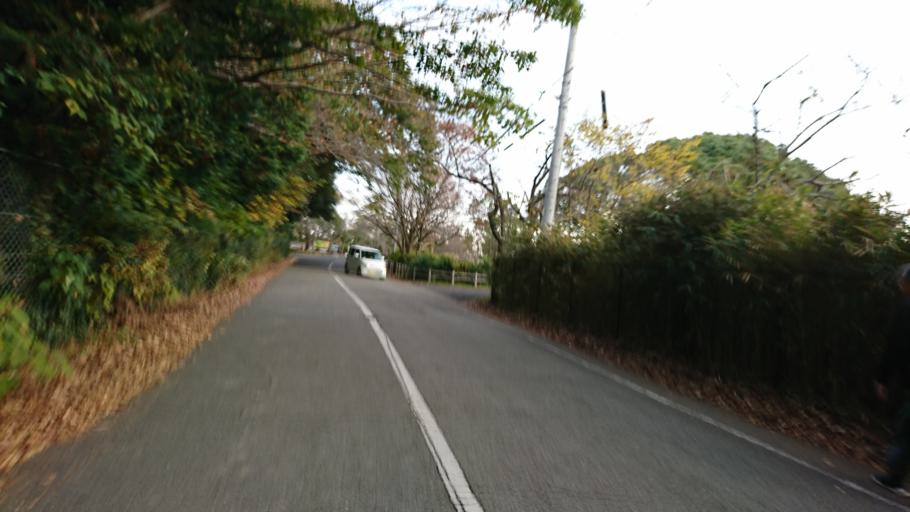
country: JP
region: Hyogo
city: Kakogawacho-honmachi
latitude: 34.7825
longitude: 134.8644
